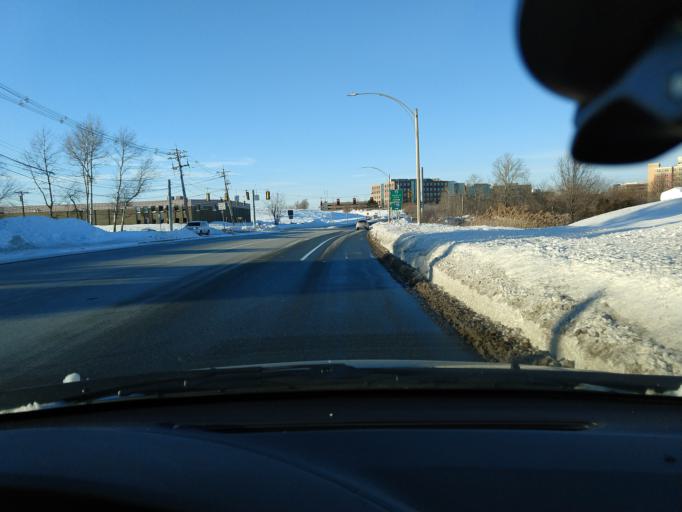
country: US
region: Massachusetts
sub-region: Middlesex County
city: Woburn
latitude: 42.5174
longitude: -71.1379
